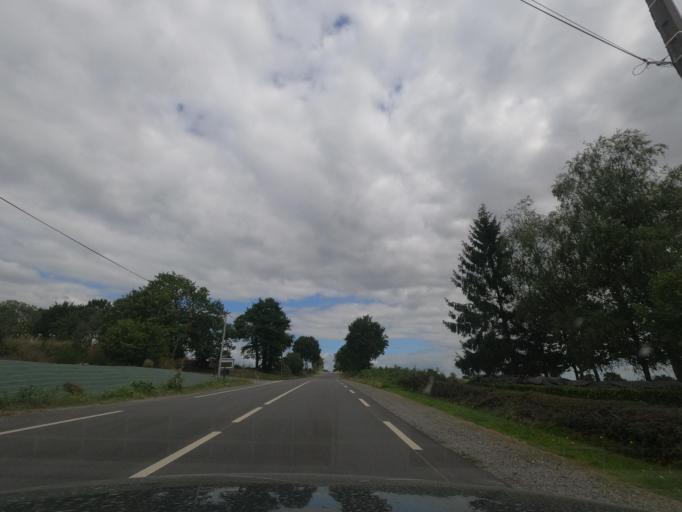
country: FR
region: Brittany
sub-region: Departement d'Ille-et-Vilaine
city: Saint-Jean-sur-Couesnon
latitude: 48.3035
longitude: -1.3555
